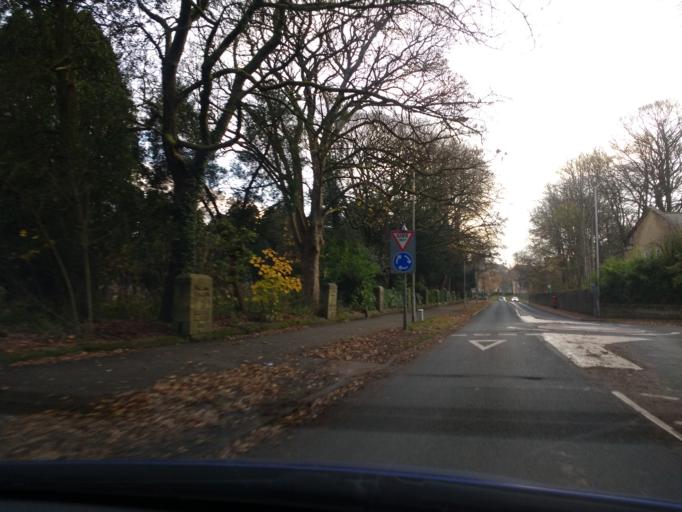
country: GB
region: England
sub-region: Lancashire
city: Lancaster
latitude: 54.0489
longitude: -2.7781
